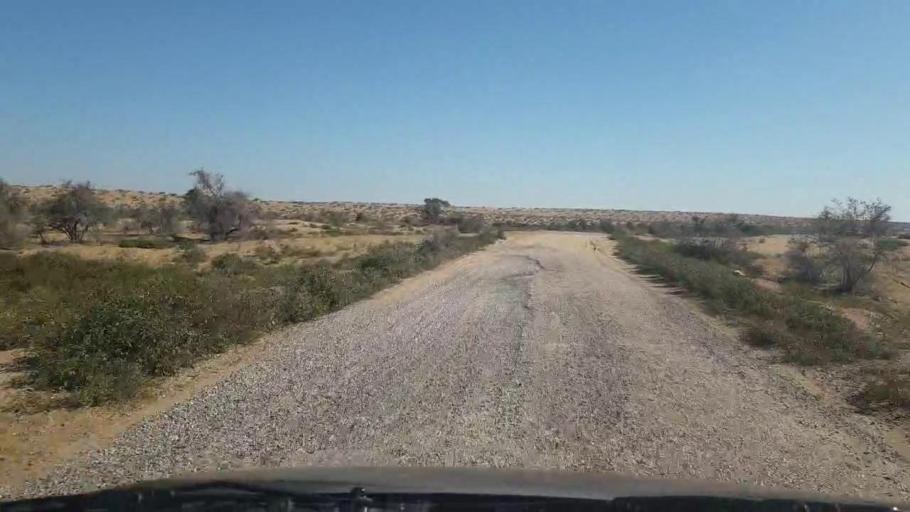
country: PK
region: Sindh
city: Bozdar
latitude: 27.0120
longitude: 68.7948
